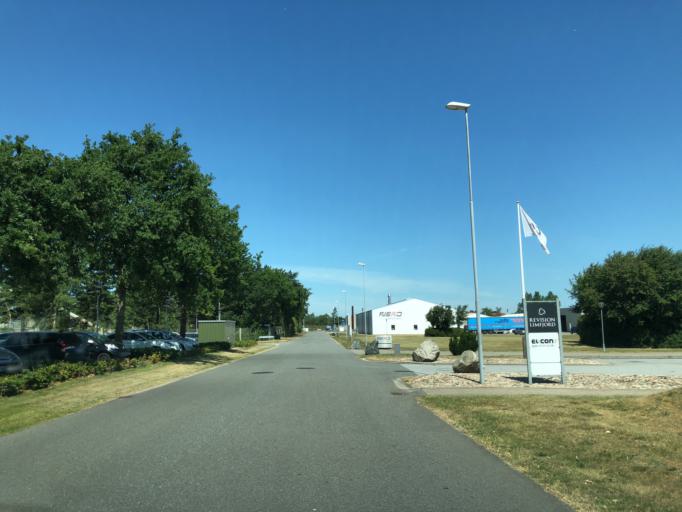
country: DK
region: Central Jutland
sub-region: Skive Kommune
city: Skive
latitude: 56.5361
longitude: 9.0344
